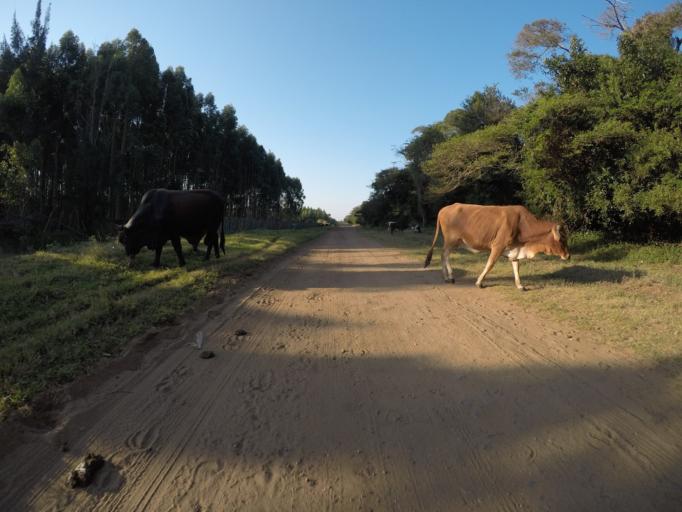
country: ZA
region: KwaZulu-Natal
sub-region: uThungulu District Municipality
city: KwaMbonambi
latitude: -28.6983
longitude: 32.1942
